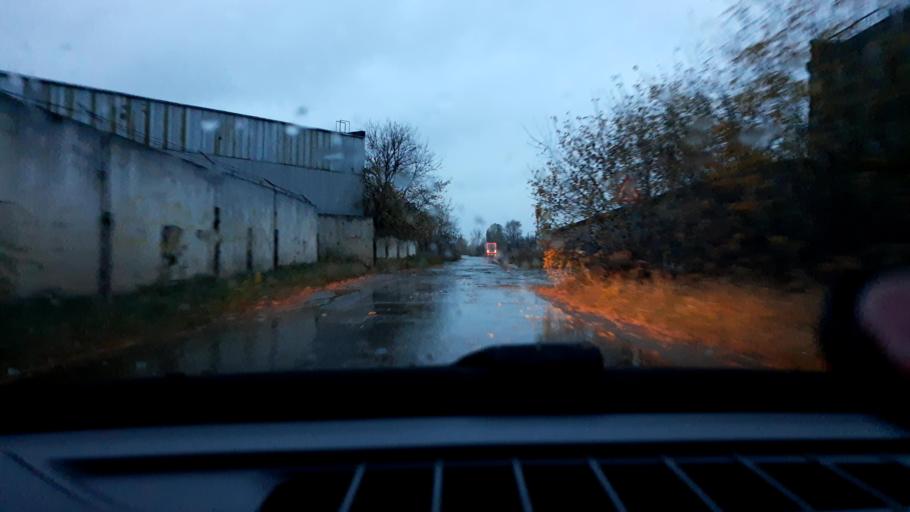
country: RU
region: Nizjnij Novgorod
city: Gorbatovka
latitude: 56.3386
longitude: 43.8187
